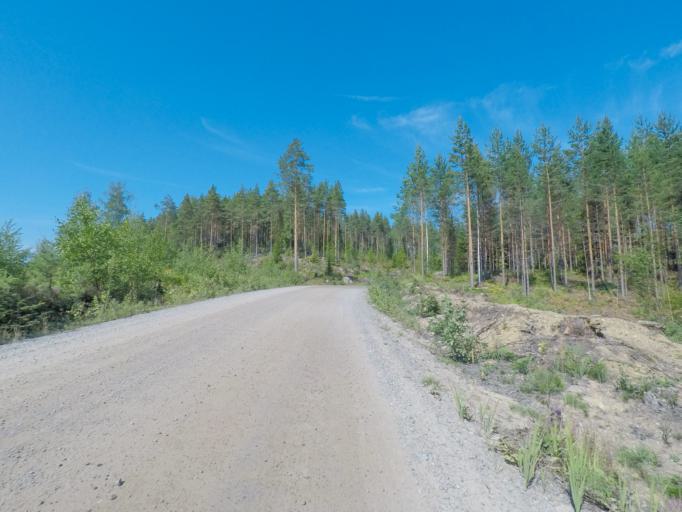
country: FI
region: Southern Savonia
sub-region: Mikkeli
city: Puumala
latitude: 61.4061
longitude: 28.0468
